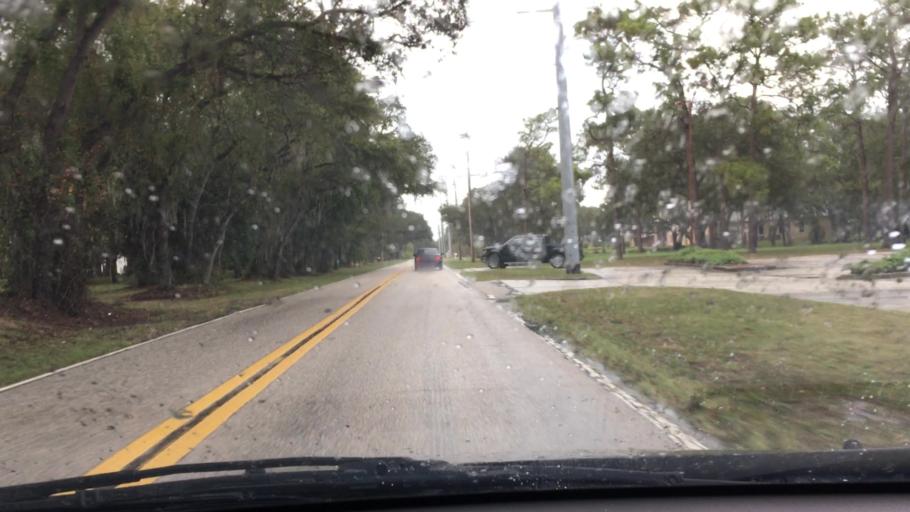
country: US
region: Florida
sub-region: Hillsborough County
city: Thonotosassa
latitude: 28.0475
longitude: -82.3436
